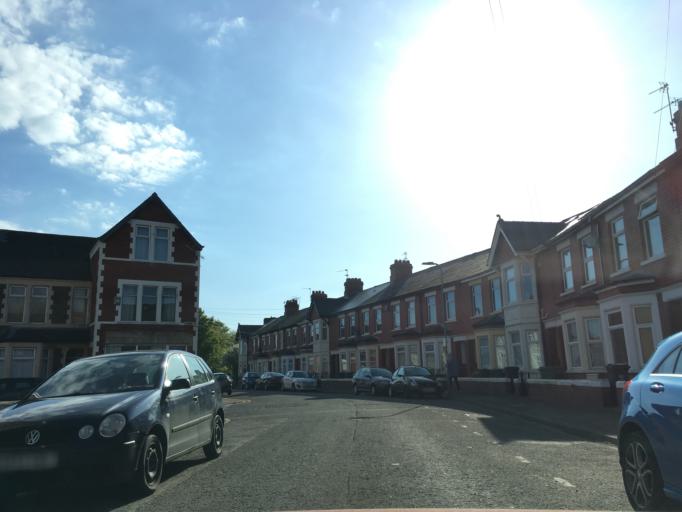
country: GB
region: Wales
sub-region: Cardiff
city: Cardiff
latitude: 51.4973
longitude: -3.1866
